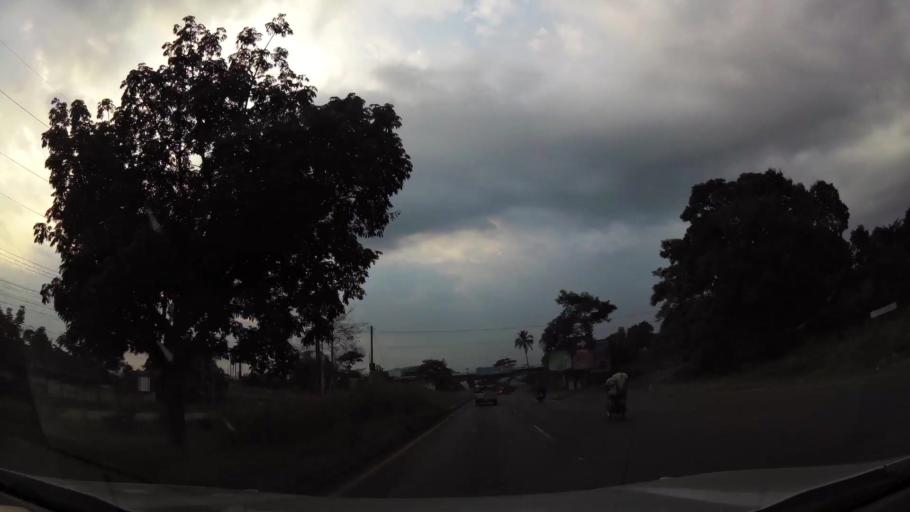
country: GT
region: Escuintla
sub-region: Municipio de Escuintla
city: Escuintla
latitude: 14.2820
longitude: -90.7862
